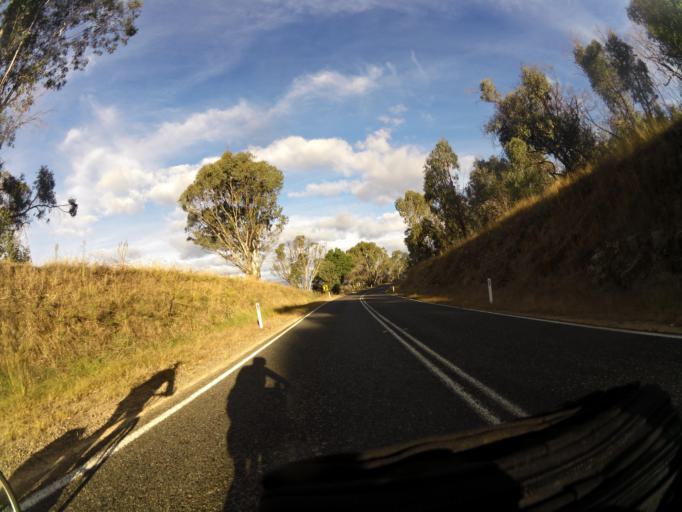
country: AU
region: New South Wales
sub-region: Greater Hume Shire
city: Holbrook
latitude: -36.0093
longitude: 147.9067
